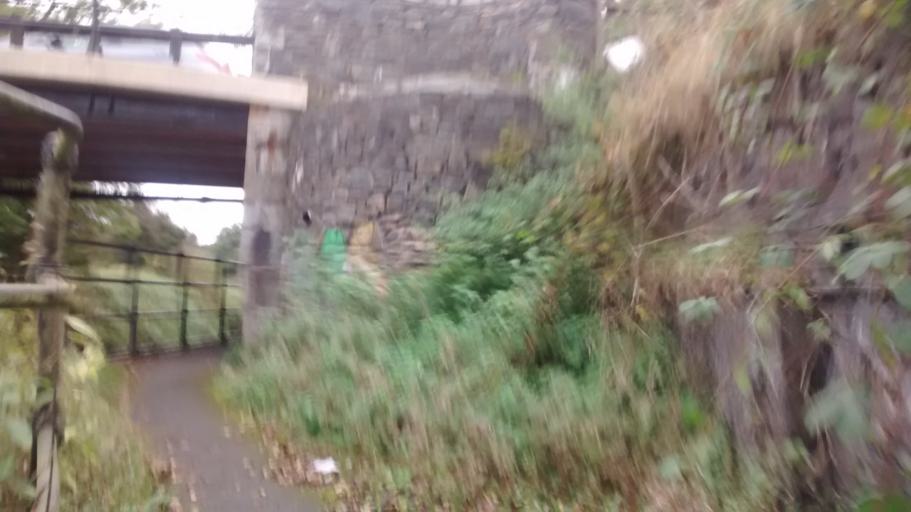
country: GB
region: Northern Ireland
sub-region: Armagh District
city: Tandragee
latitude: 54.3956
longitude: -6.4015
